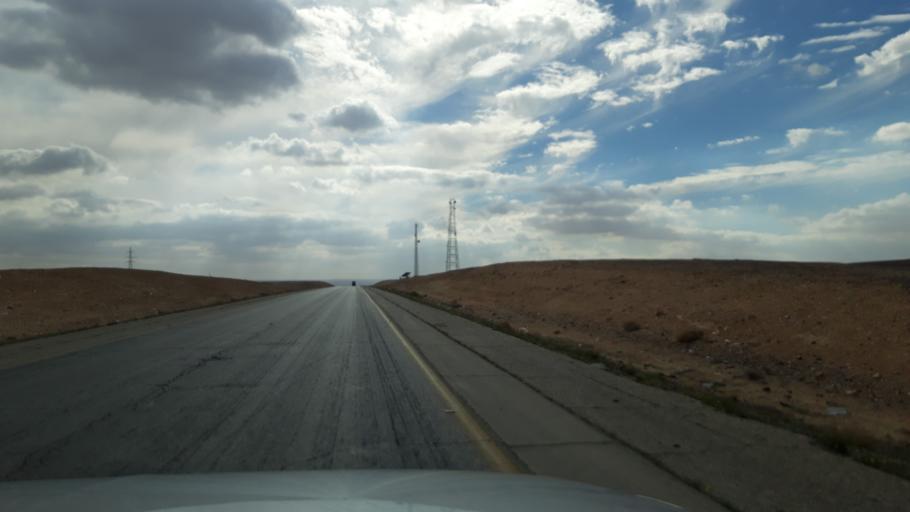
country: JO
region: Amman
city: Al Azraq ash Shamali
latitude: 31.7387
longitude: 36.5245
